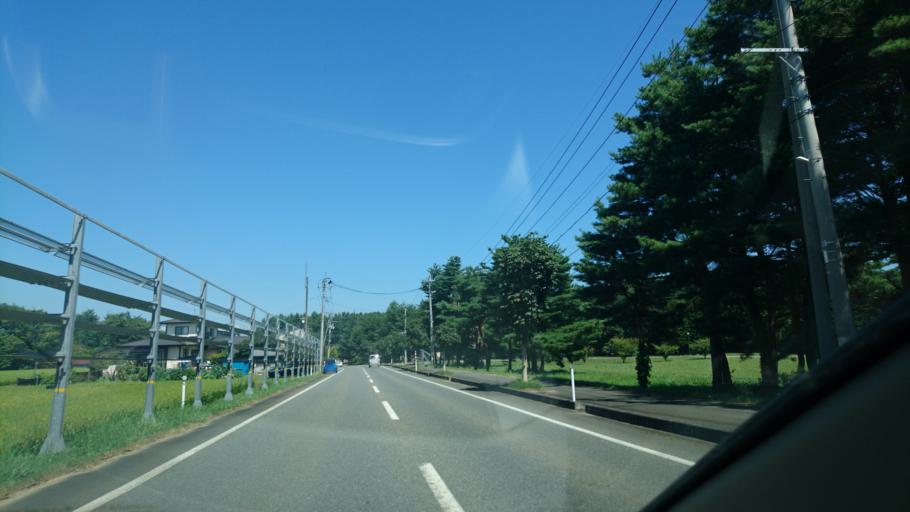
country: JP
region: Iwate
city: Kitakami
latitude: 39.2607
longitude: 141.0865
